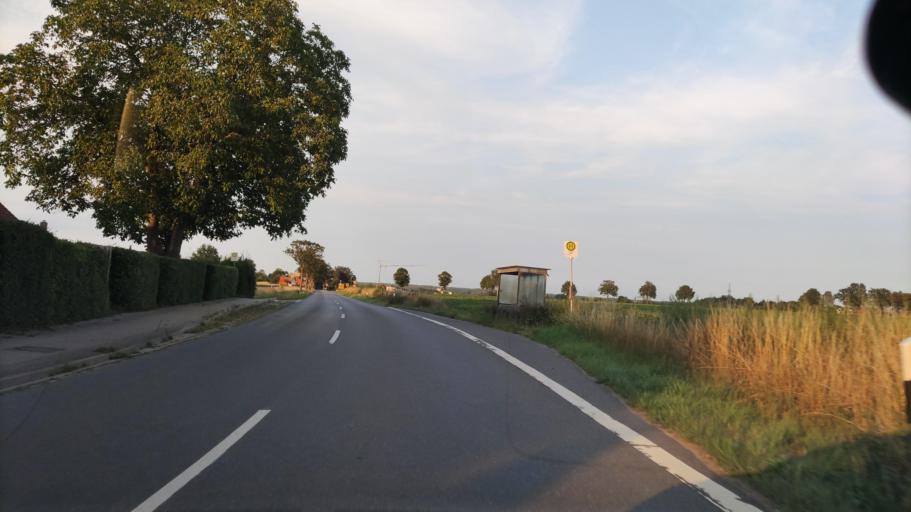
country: DE
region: Lower Saxony
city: Bad Bevensen
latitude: 53.0720
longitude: 10.5593
